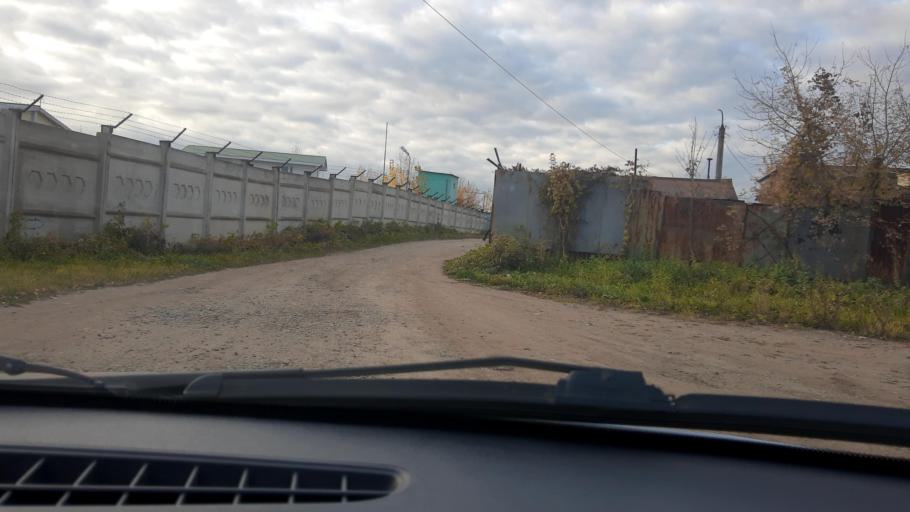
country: RU
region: Bashkortostan
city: Ufa
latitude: 54.7490
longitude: 55.9134
